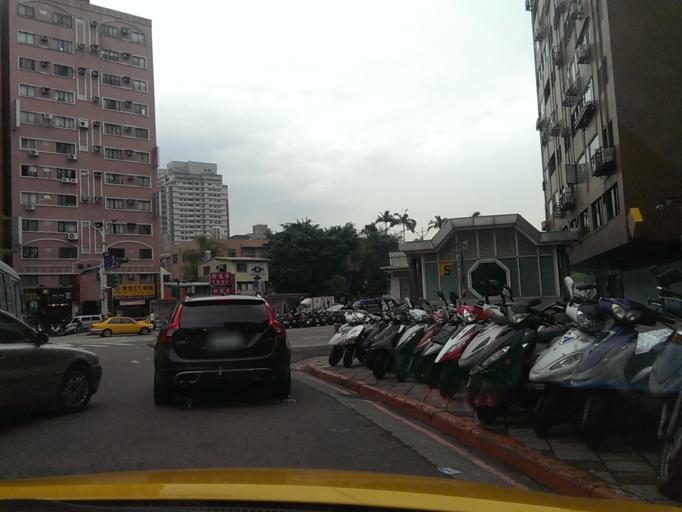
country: TW
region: Taipei
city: Taipei
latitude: 25.0207
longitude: 121.5274
